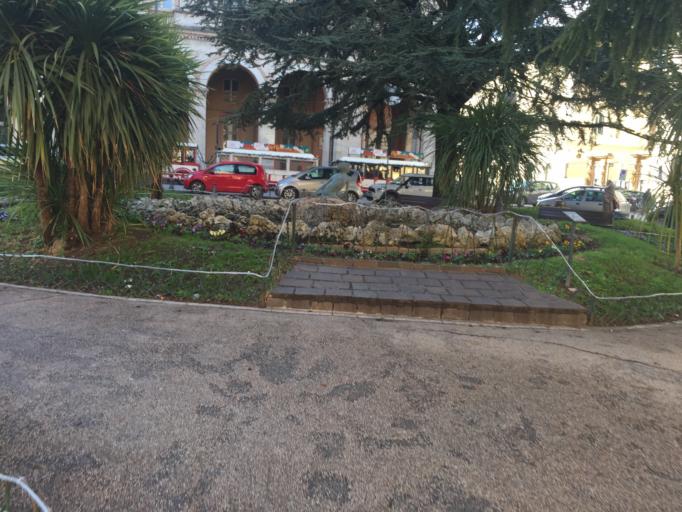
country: IT
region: Umbria
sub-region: Provincia di Perugia
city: Perugia
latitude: 43.1092
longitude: 12.3883
